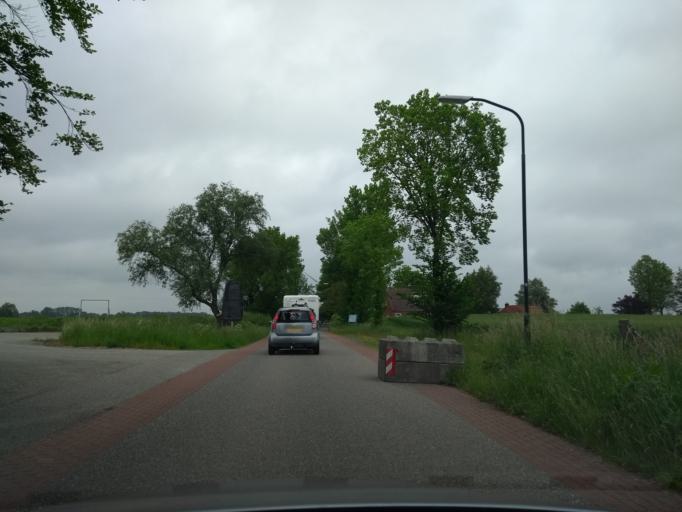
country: NL
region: Groningen
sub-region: Gemeente Zuidhorn
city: Oldehove
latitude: 53.3288
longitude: 6.4267
